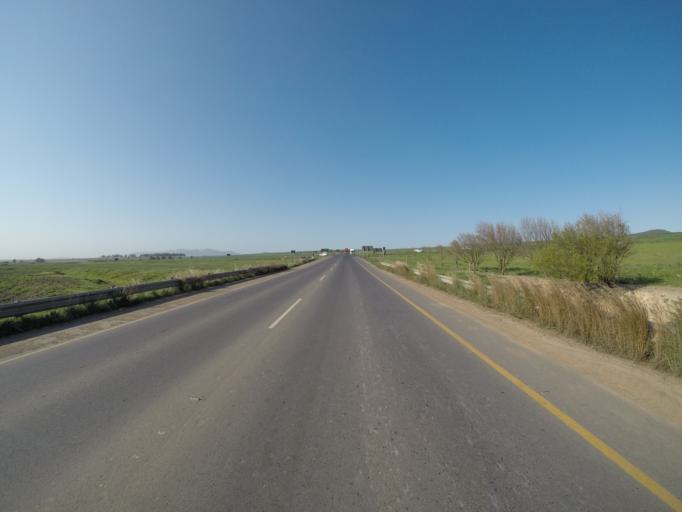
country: ZA
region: Western Cape
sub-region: City of Cape Town
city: Kraaifontein
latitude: -33.7702
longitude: 18.7552
